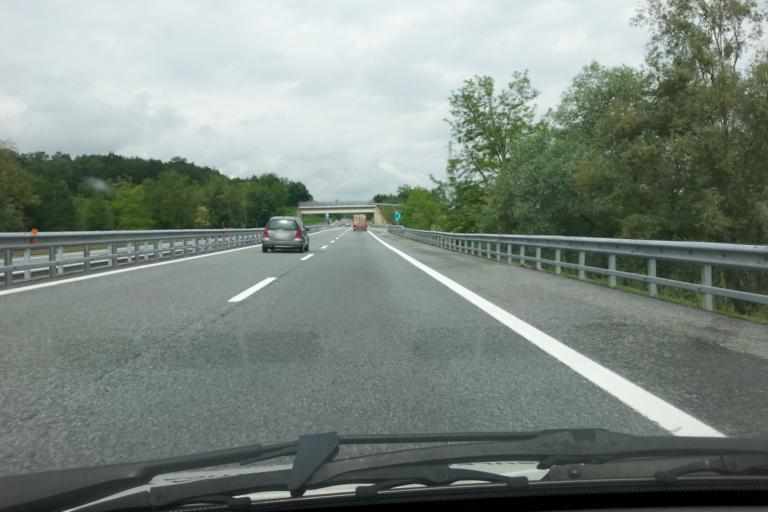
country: IT
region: Piedmont
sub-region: Provincia di Cuneo
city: Lesegno
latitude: 44.3928
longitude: 7.9925
